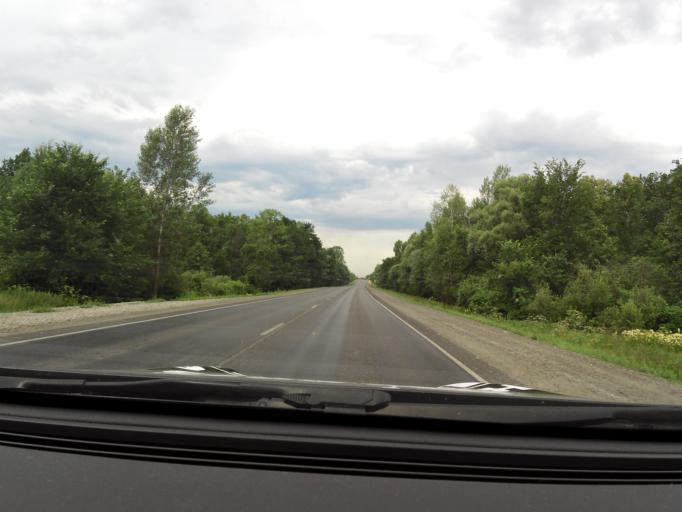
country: RU
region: Bashkortostan
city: Urman
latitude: 54.8275
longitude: 56.9140
